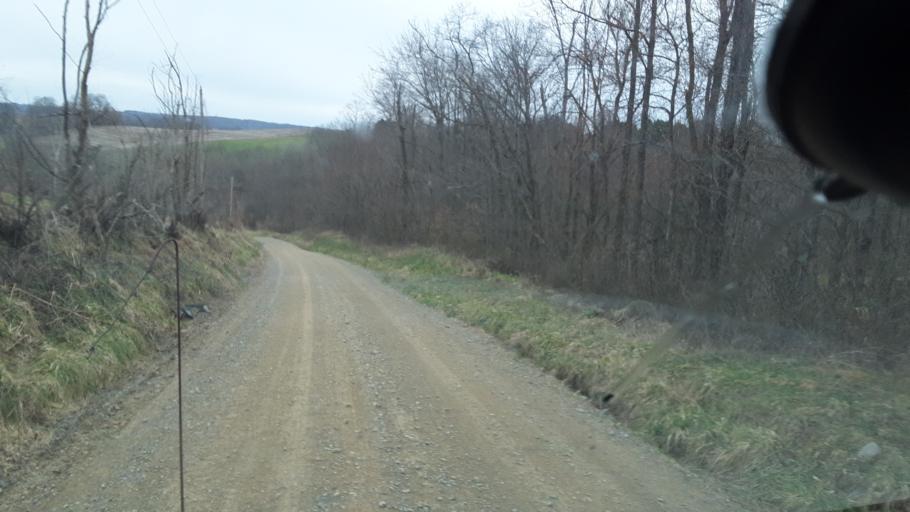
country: US
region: Ohio
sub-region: Coshocton County
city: West Lafayette
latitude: 40.3394
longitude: -81.7096
